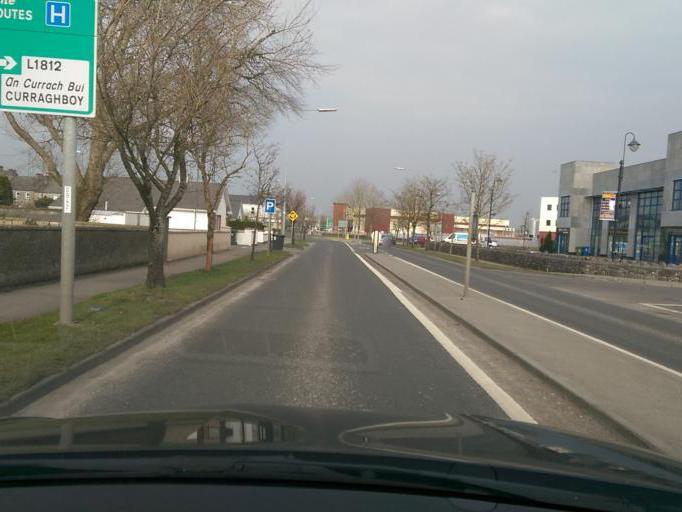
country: IE
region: Connaught
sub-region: Roscommon
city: Roscommon
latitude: 53.6273
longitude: -8.1899
